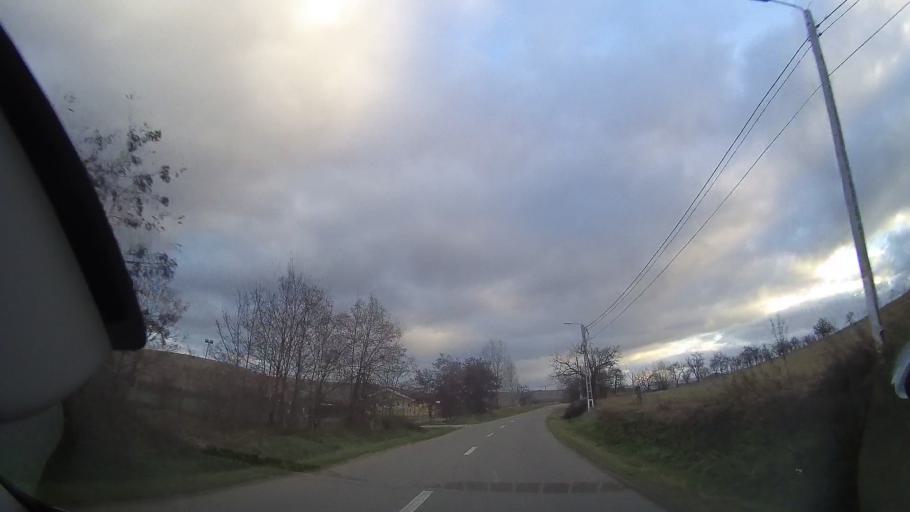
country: RO
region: Cluj
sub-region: Comuna Sancraiu
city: Sancraiu
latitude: 46.8253
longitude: 22.9909
